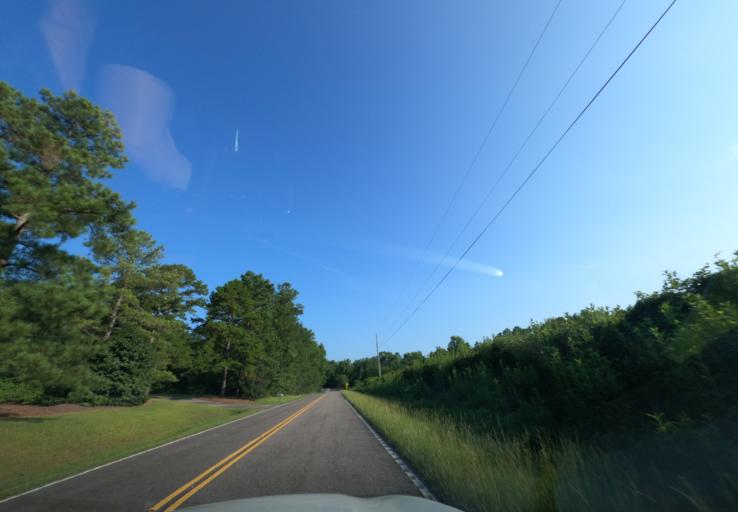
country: US
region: South Carolina
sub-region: Edgefield County
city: Murphys Estates
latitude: 33.6215
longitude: -81.9695
